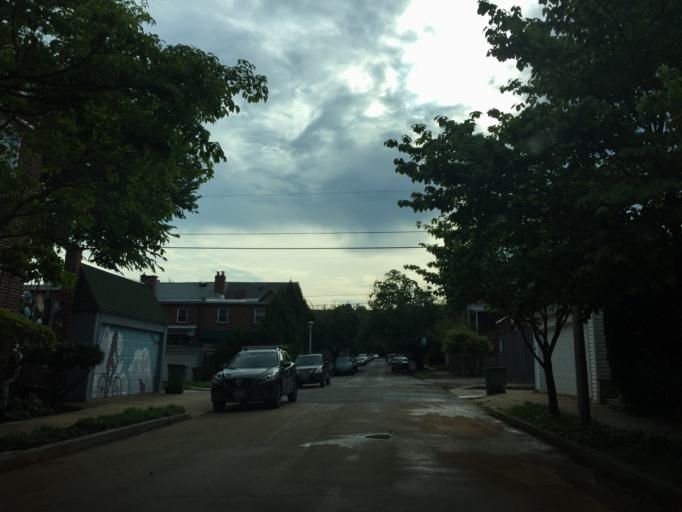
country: US
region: Maryland
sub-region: City of Baltimore
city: Baltimore
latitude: 39.3339
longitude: -76.6259
